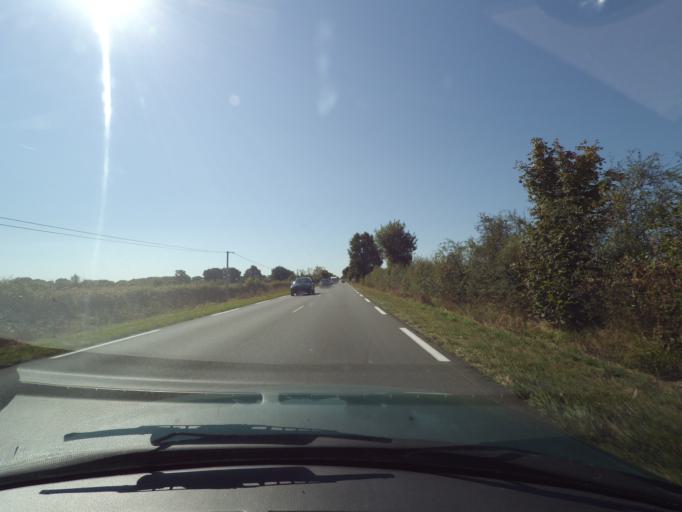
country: FR
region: Poitou-Charentes
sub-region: Departement de la Vienne
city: Saulge
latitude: 46.3145
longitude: 0.8263
